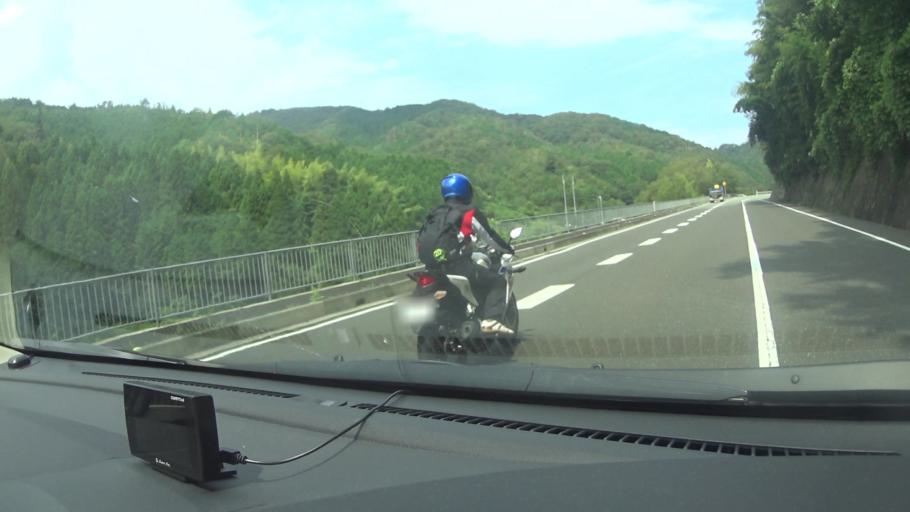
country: JP
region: Kyoto
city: Ayabe
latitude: 35.2626
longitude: 135.2724
